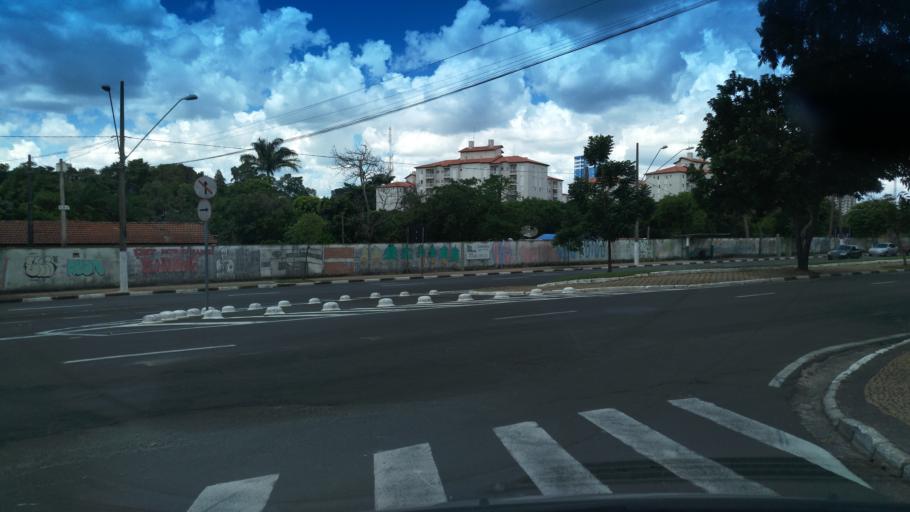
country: BR
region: Sao Paulo
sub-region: Valinhos
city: Valinhos
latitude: -22.9791
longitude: -46.9903
